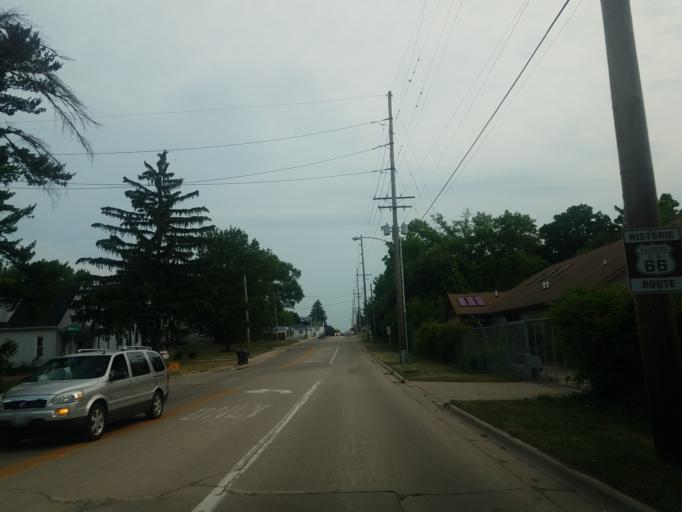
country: US
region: Illinois
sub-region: McLean County
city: Bloomington
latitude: 40.4695
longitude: -89.0063
